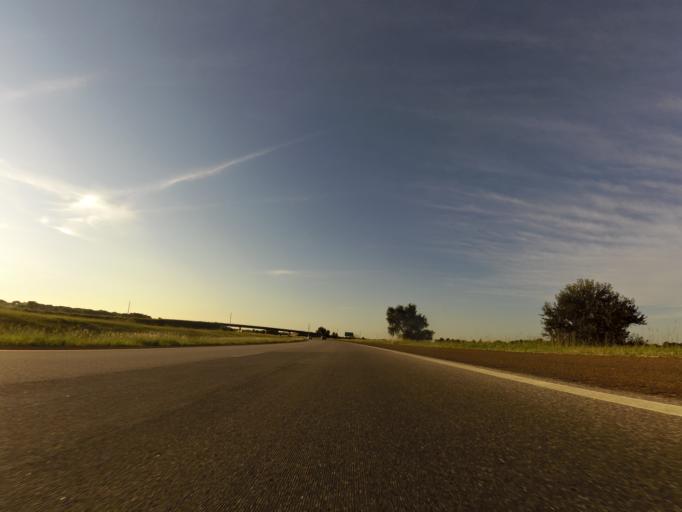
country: US
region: Kansas
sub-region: Sedgwick County
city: Maize
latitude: 37.7631
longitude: -97.4476
